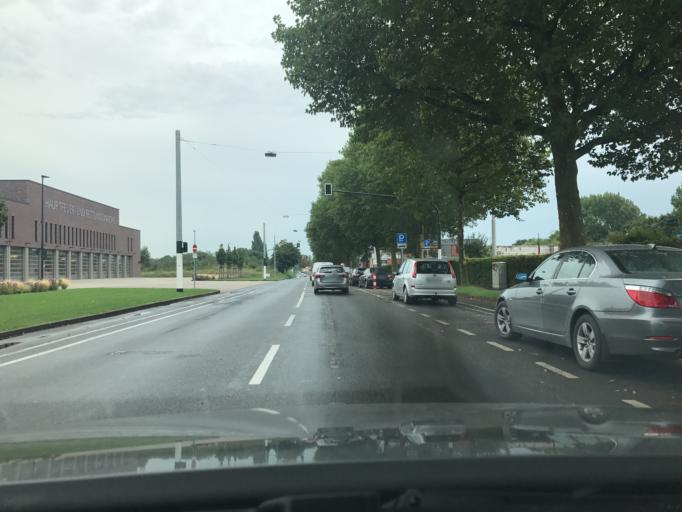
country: DE
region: North Rhine-Westphalia
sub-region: Regierungsbezirk Dusseldorf
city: Krefeld
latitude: 51.3281
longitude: 6.5834
